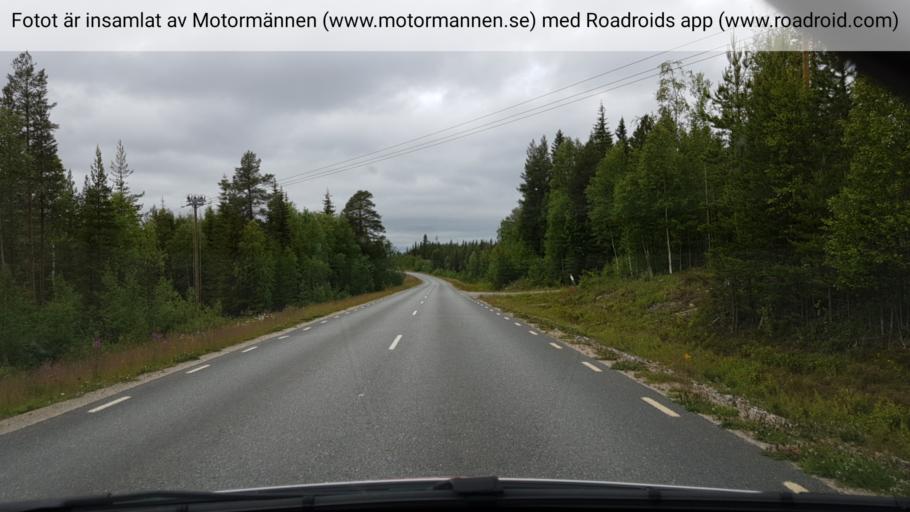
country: SE
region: Vaesterbotten
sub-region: Lycksele Kommun
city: Lycksele
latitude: 64.5061
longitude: 18.9486
